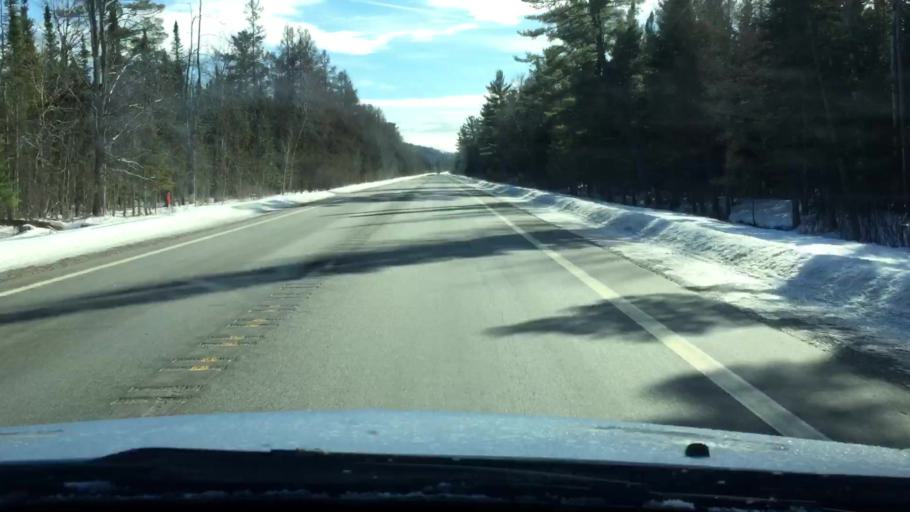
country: US
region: Michigan
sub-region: Antrim County
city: Mancelona
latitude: 45.0265
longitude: -85.0659
